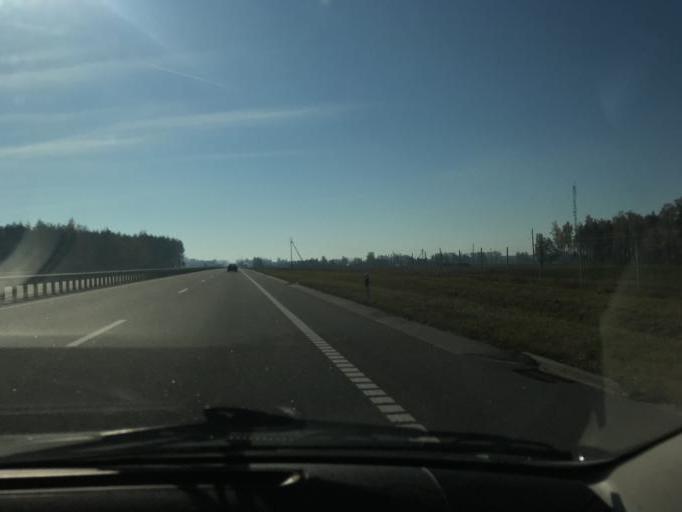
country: BY
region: Minsk
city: Slutsk
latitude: 53.2340
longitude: 27.5503
